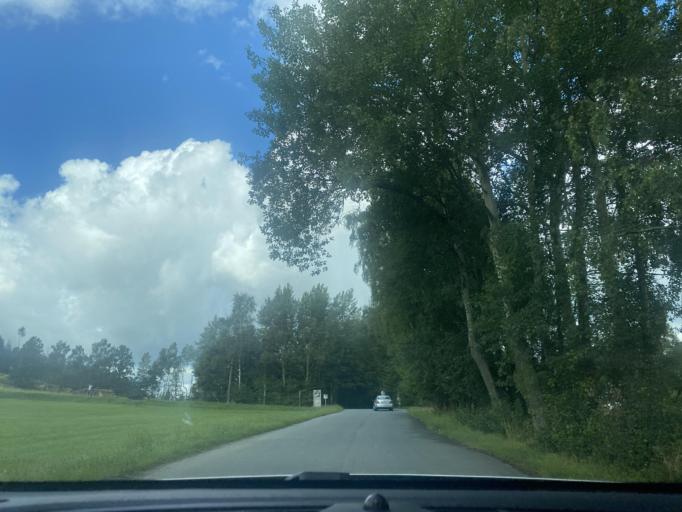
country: DE
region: Saxony
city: Beiersdorf
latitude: 51.0806
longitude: 14.5272
